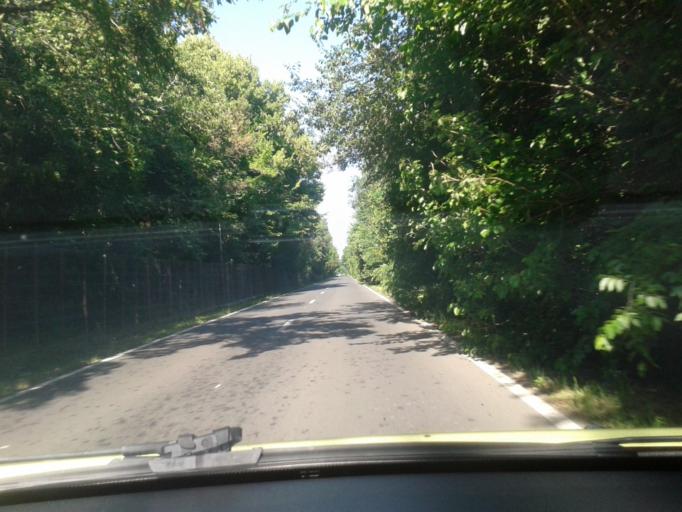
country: RO
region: Constanta
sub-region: Comuna Douazeci si Trei August
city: Douazeci si Trei August
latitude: 43.8751
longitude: 28.5929
